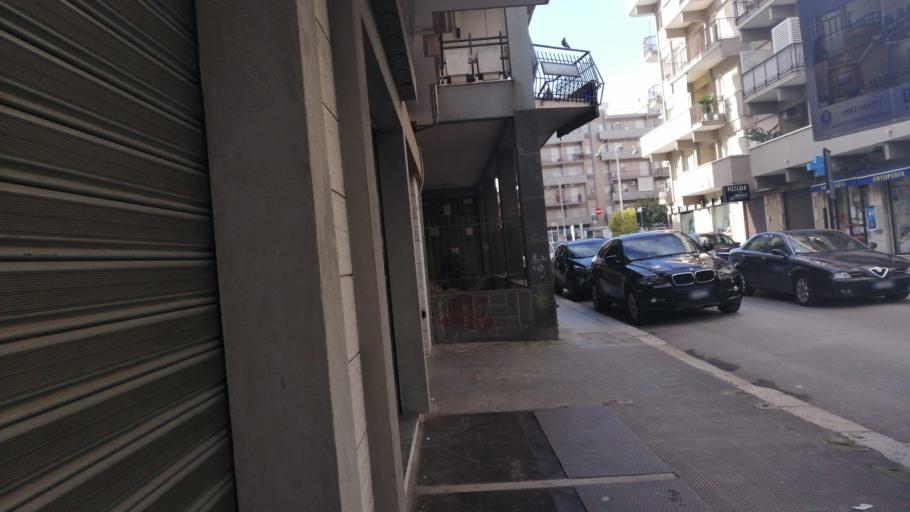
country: IT
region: Apulia
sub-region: Provincia di Barletta - Andria - Trani
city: Andria
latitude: 41.2320
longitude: 16.3002
